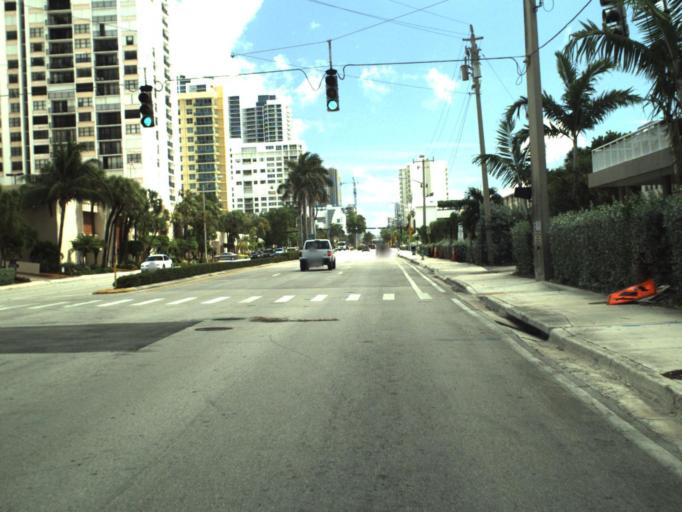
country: US
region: Florida
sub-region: Broward County
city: Hollywood
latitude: 26.0000
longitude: -80.1181
